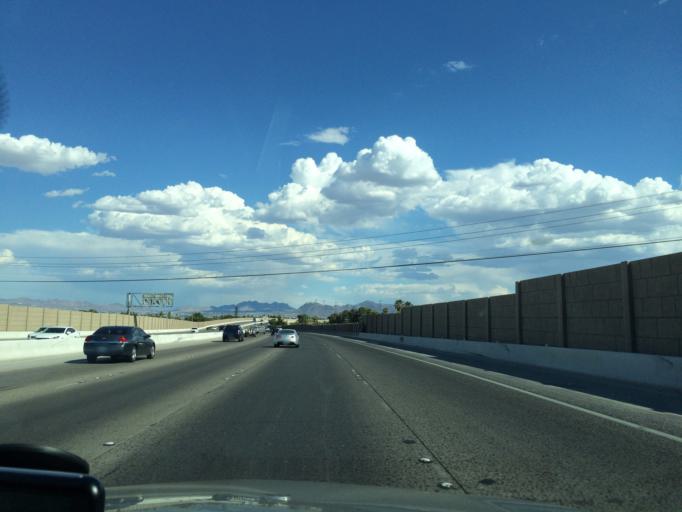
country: US
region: Nevada
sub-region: Clark County
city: Winchester
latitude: 36.1284
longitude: -115.0884
